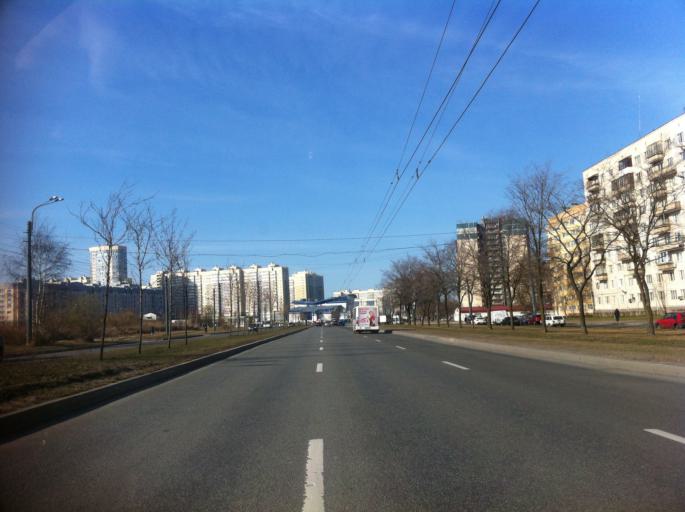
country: RU
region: St.-Petersburg
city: Uritsk
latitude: 59.8547
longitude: 30.1761
